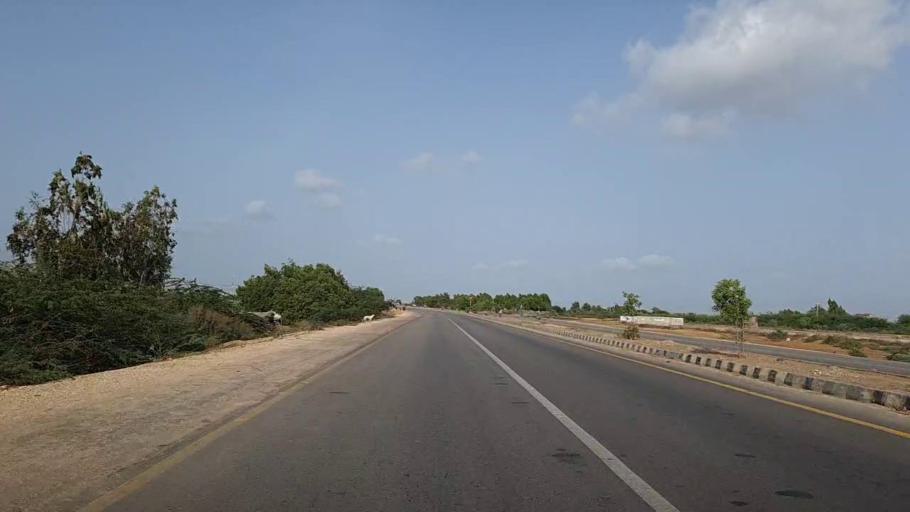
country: PK
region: Sindh
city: Thatta
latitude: 24.7397
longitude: 67.7577
